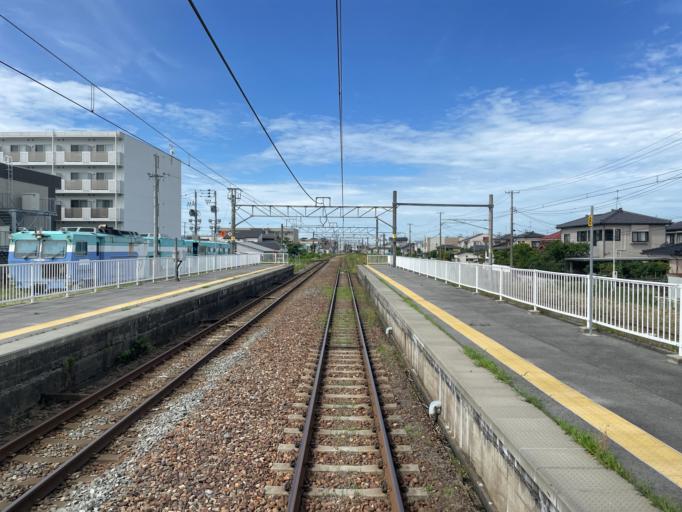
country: JP
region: Niigata
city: Suibara
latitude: 37.9192
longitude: 139.2151
